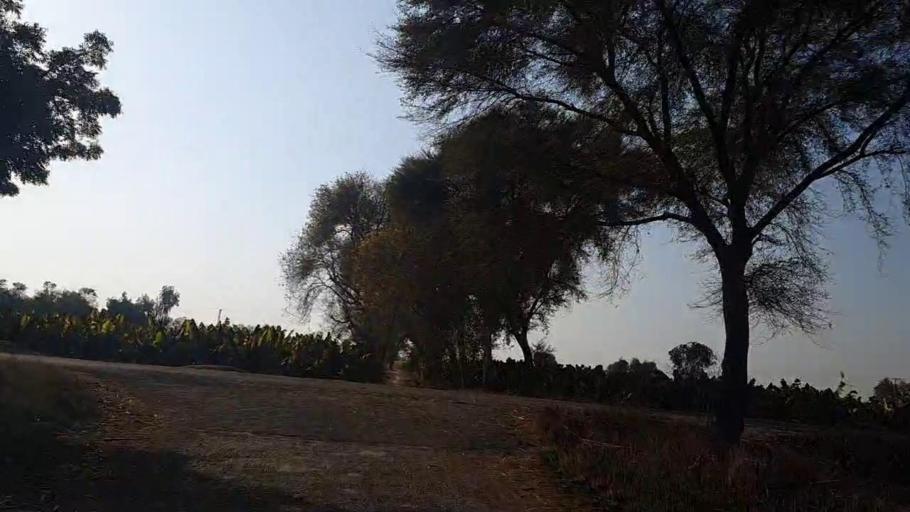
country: PK
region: Sindh
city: Daur
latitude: 26.3328
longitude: 68.1466
